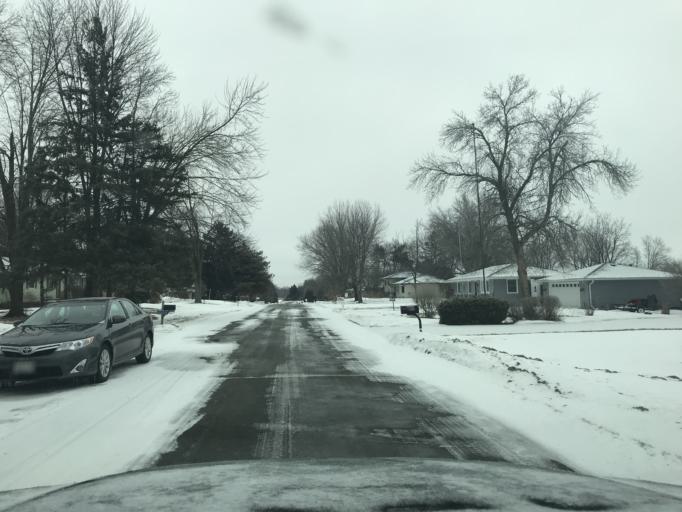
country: US
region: Wisconsin
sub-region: Dane County
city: Cottage Grove
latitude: 43.0972
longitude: -89.2367
